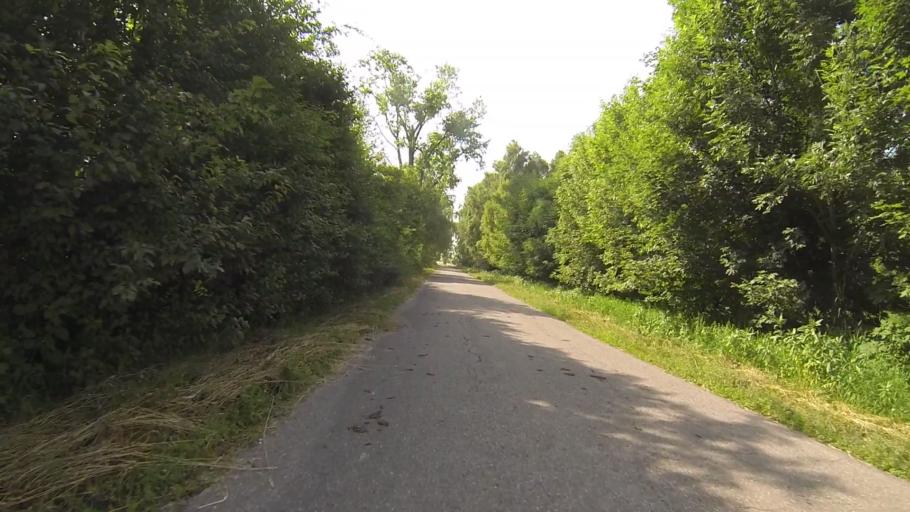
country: DE
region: Baden-Wuerttemberg
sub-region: Tuebingen Region
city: Asselfingen
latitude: 48.4957
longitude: 10.1982
